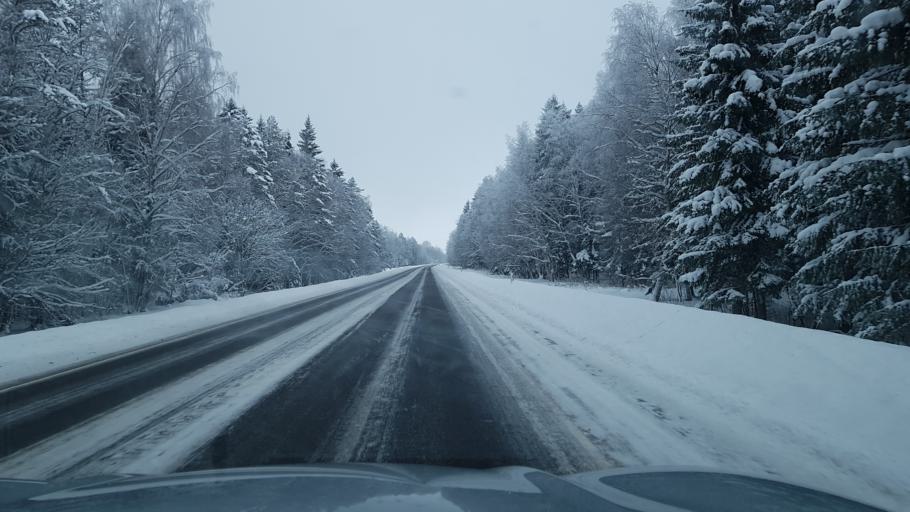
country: EE
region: Ida-Virumaa
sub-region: Johvi vald
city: Johvi
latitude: 59.3018
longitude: 27.3953
